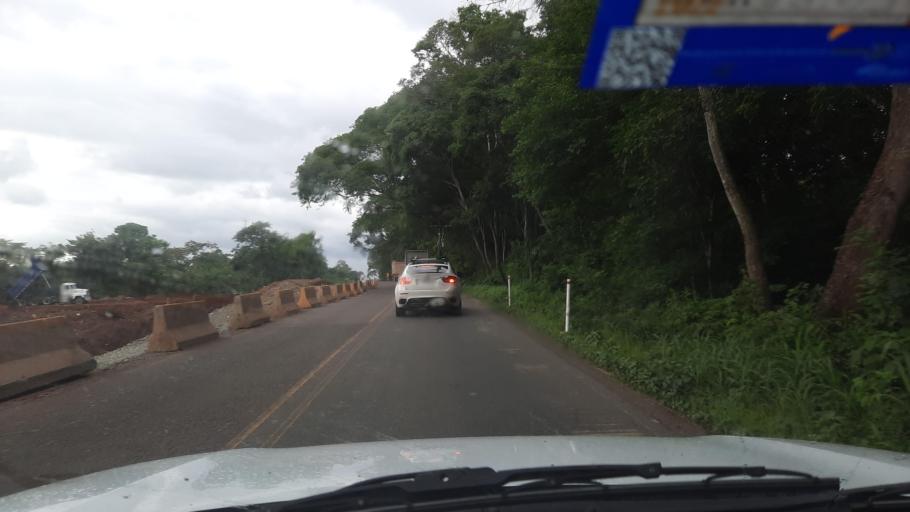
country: CR
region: Puntarenas
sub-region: Canton Central de Puntarenas
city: Puntarenas
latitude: 10.1174
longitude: -84.8958
